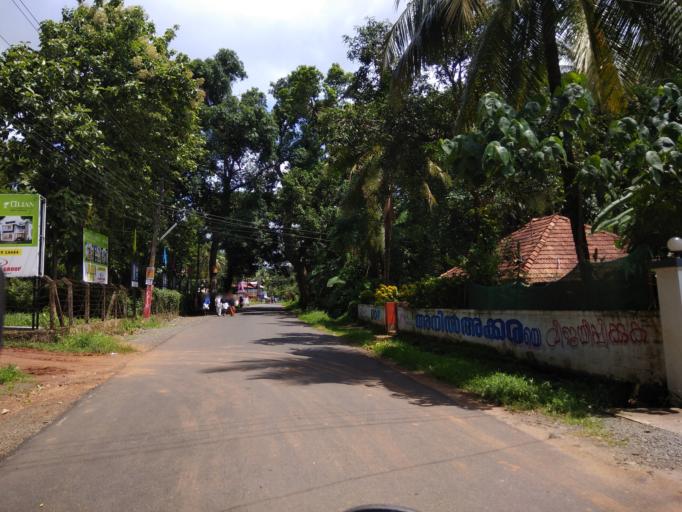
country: IN
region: Kerala
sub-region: Thrissur District
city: Avanoor
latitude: 10.5477
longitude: 76.1485
